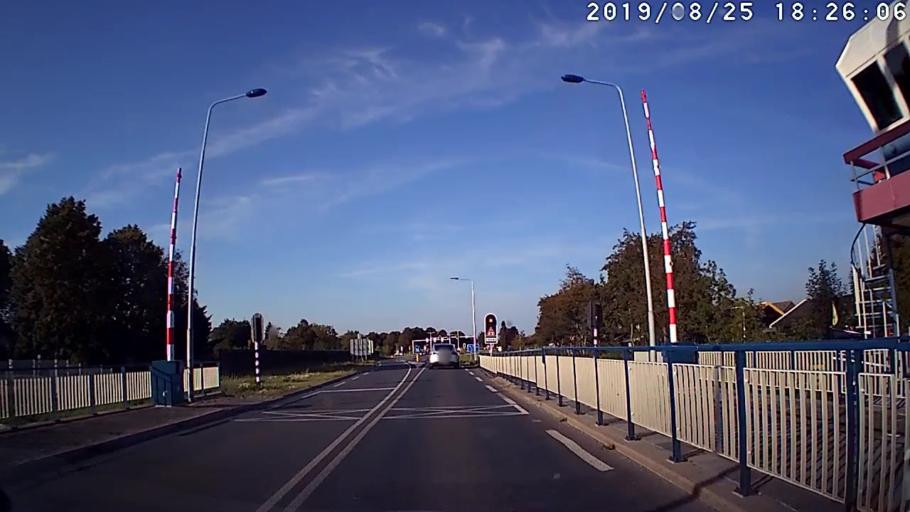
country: NL
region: Friesland
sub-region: Gemeente Lemsterland
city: Lemmer
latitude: 52.8464
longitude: 5.6998
